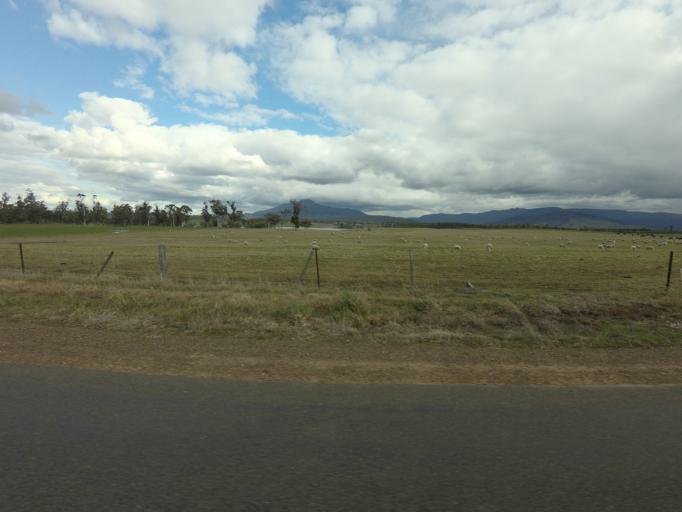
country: AU
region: Tasmania
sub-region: Northern Midlands
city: Longford
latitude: -41.8059
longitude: 147.1589
